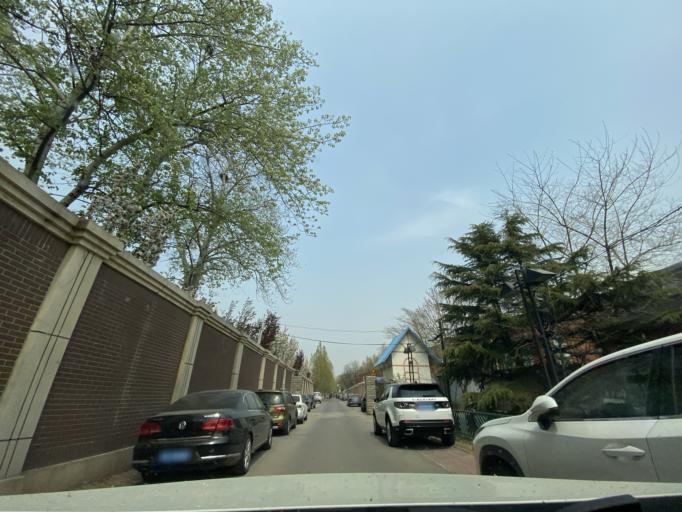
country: CN
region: Beijing
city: Sijiqing
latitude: 39.9404
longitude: 116.2457
